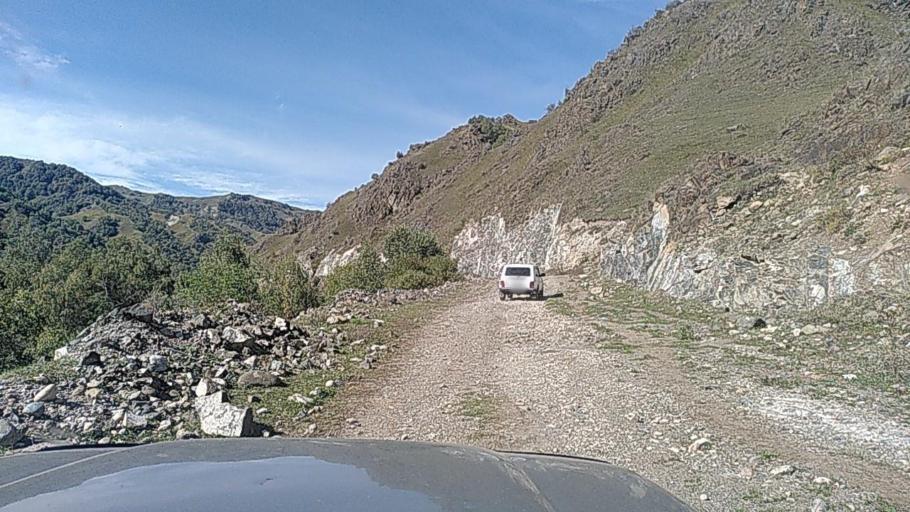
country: RU
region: Kabardino-Balkariya
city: Kamennomostskoye
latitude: 43.7208
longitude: 42.8937
